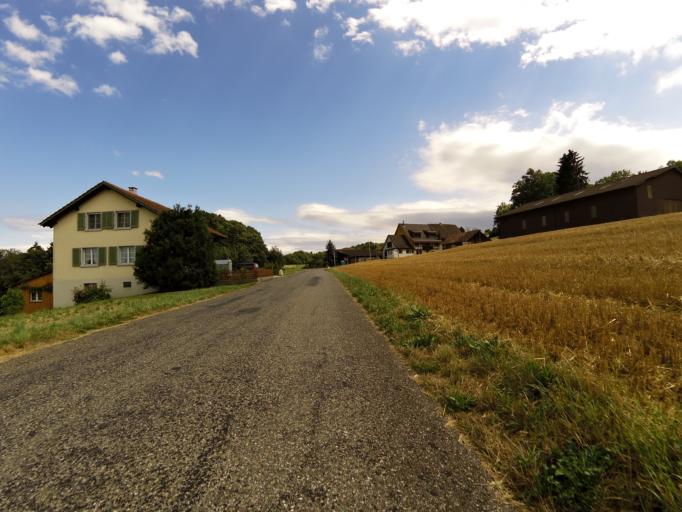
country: CH
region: Thurgau
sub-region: Kreuzlingen District
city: Ermatingen
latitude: 47.6609
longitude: 9.0802
